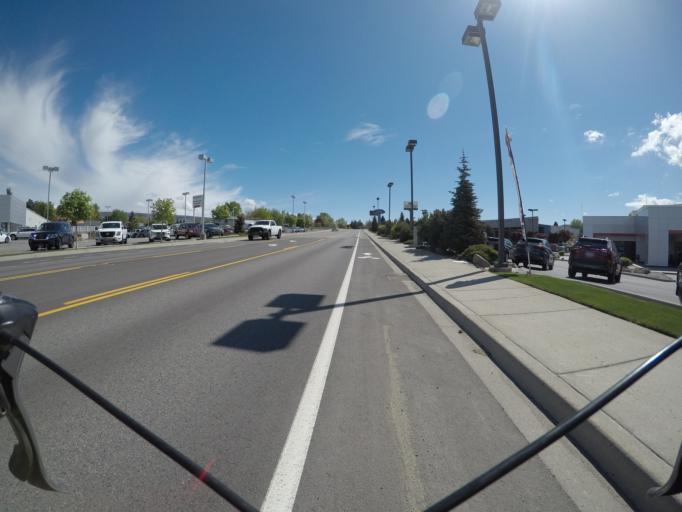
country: US
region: Washington
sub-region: Chelan County
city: South Wenatchee
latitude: 47.4002
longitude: -120.2794
